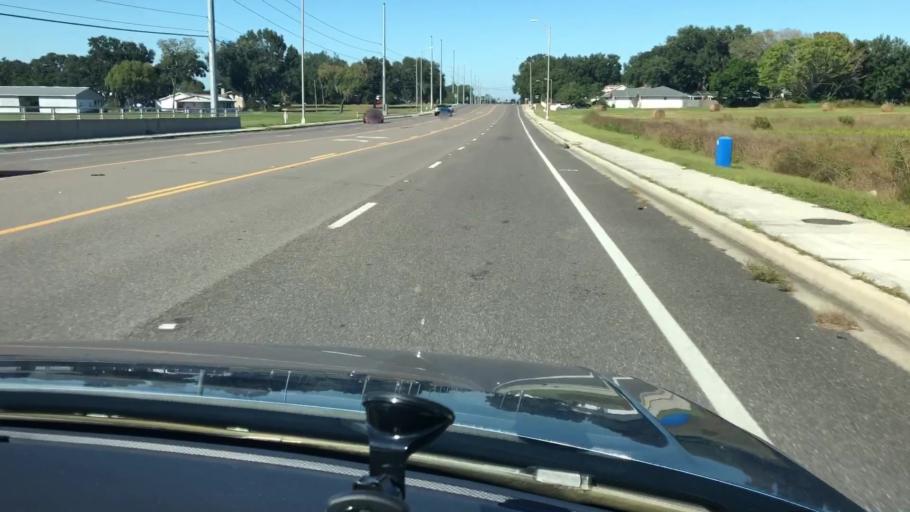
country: US
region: Florida
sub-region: Polk County
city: Kathleen
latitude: 28.1300
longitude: -82.0233
